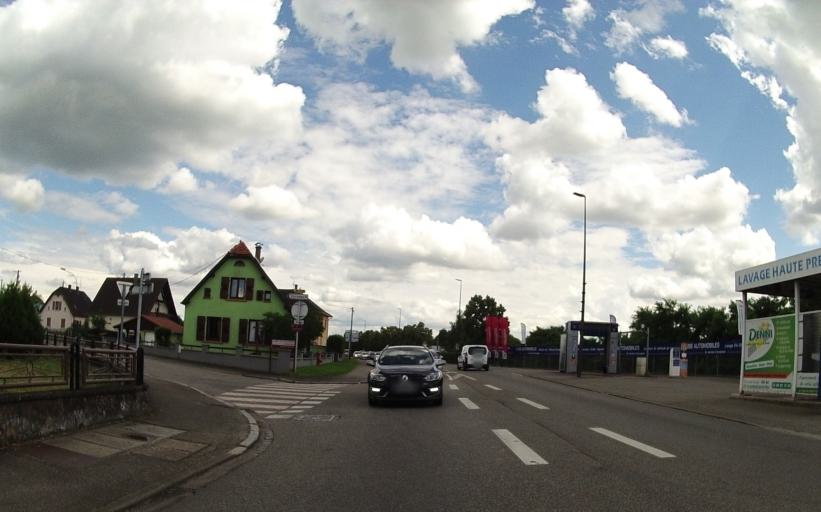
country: FR
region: Alsace
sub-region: Departement du Bas-Rhin
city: Mertzwiller
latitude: 48.8684
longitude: 7.6878
